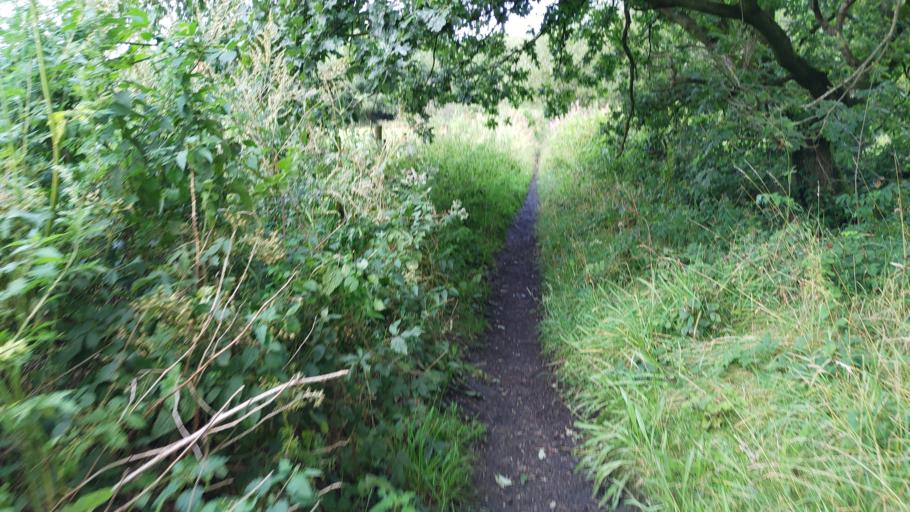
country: GB
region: England
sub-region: Lancashire
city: Coppull
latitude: 53.6290
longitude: -2.6623
